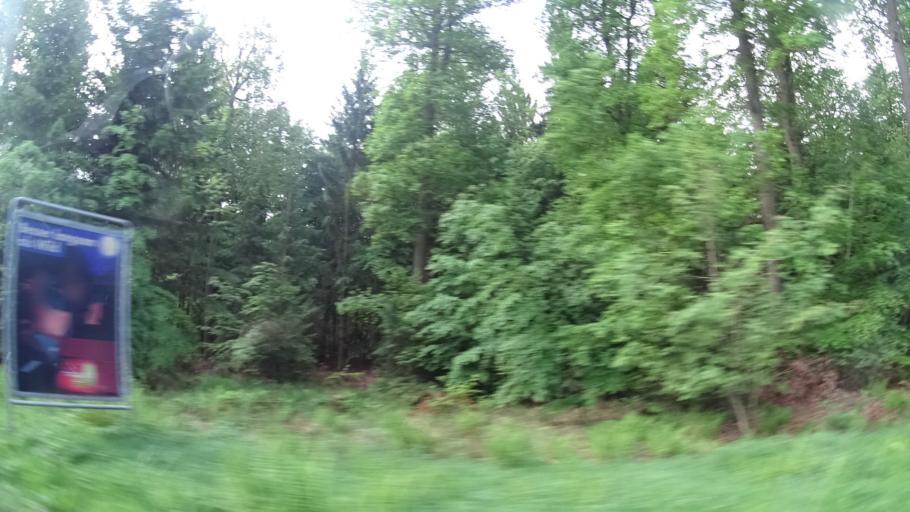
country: DE
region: Hesse
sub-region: Regierungsbezirk Darmstadt
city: Lutzelbach
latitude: 49.7340
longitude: 9.0885
